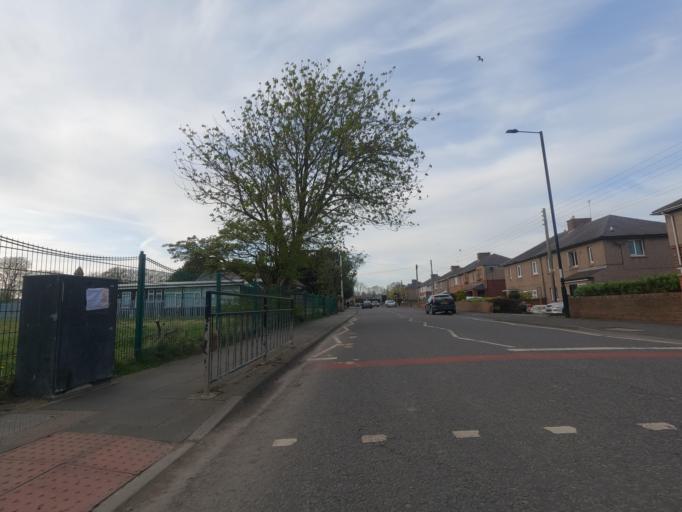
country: GB
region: England
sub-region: Newcastle upon Tyne
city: Dinnington
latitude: 55.0528
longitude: -1.6744
